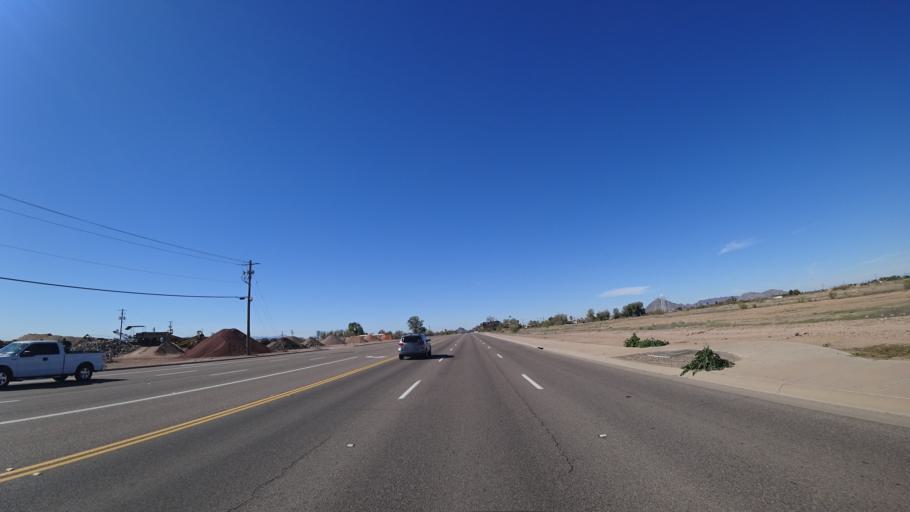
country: US
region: Arizona
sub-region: Maricopa County
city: Mesa
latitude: 33.4659
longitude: -111.8571
